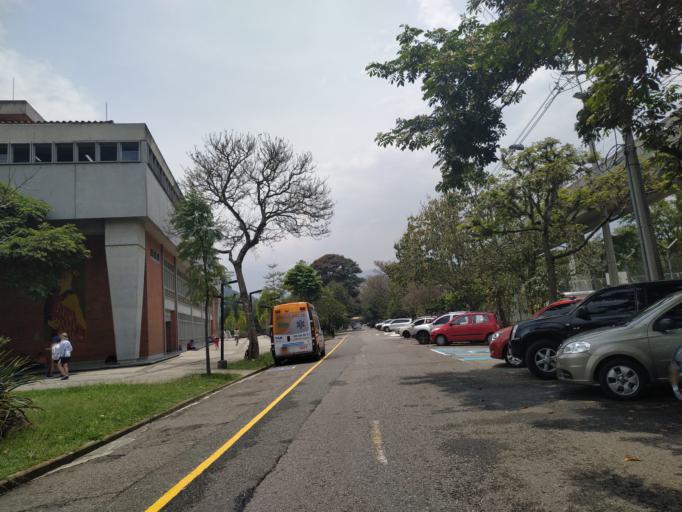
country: CO
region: Antioquia
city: Medellin
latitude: 6.2698
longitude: -75.5677
